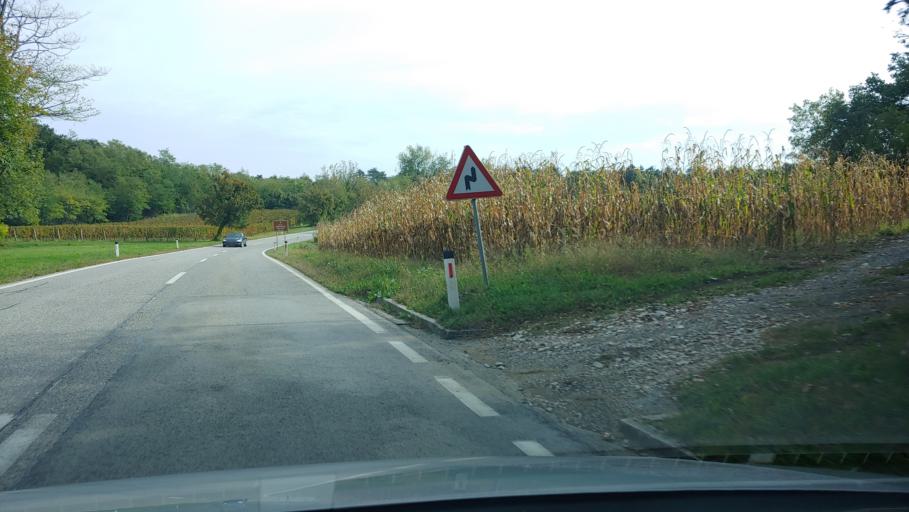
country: SI
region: Nova Gorica
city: Sempas
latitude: 45.9150
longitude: 13.7661
